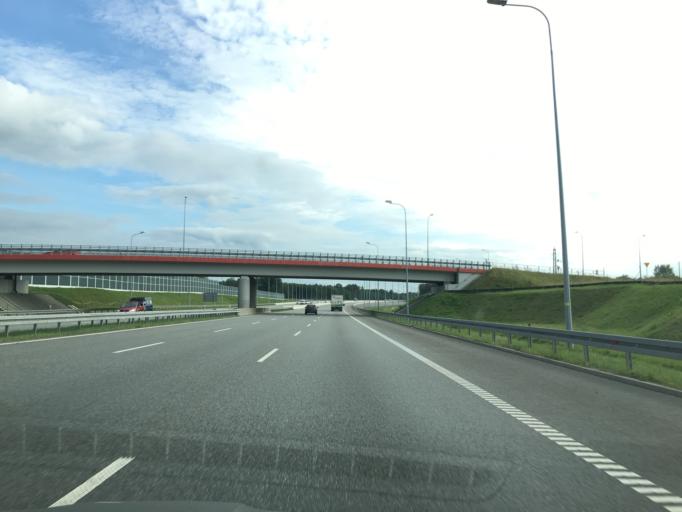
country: PL
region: Silesian Voivodeship
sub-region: Powiat tarnogorski
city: Wieszowa
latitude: 50.3367
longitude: 18.7281
